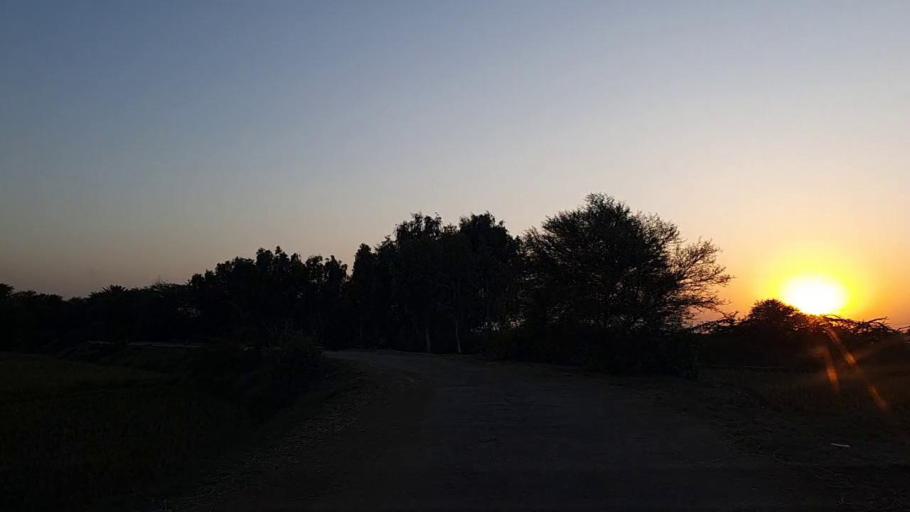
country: PK
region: Sindh
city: Mirpur Batoro
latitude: 24.6148
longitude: 68.1846
